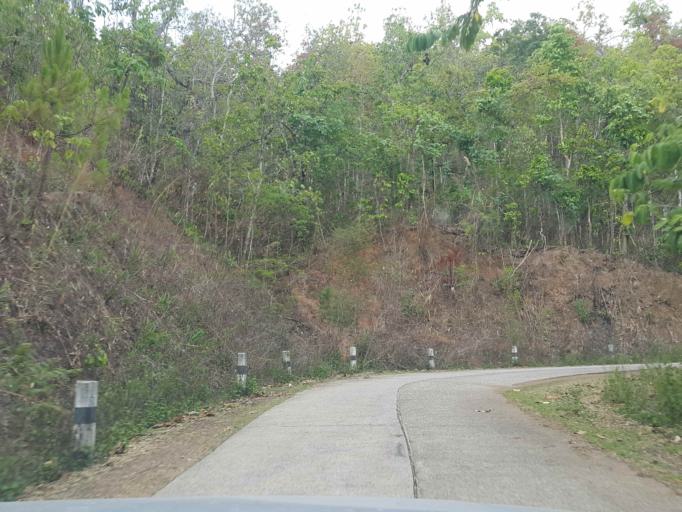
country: TH
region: Chiang Mai
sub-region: Amphoe Chiang Dao
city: Chiang Dao
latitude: 19.3789
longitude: 98.7663
